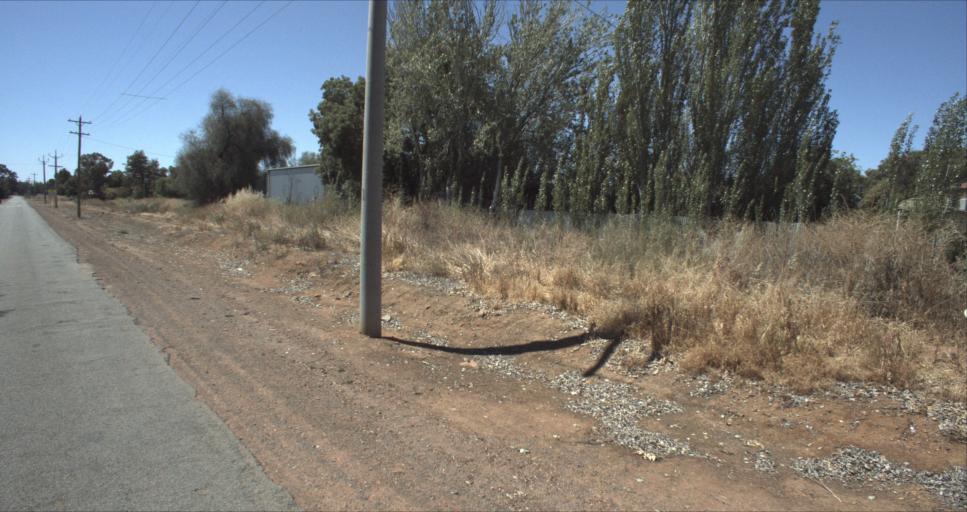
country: AU
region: New South Wales
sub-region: Leeton
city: Leeton
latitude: -34.5275
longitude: 146.3297
